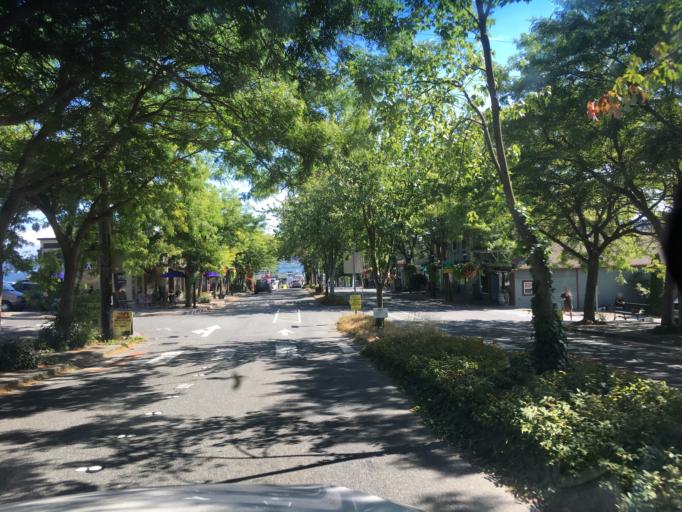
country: US
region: Washington
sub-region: Kitsap County
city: Kingston
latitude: 47.7979
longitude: -122.4975
